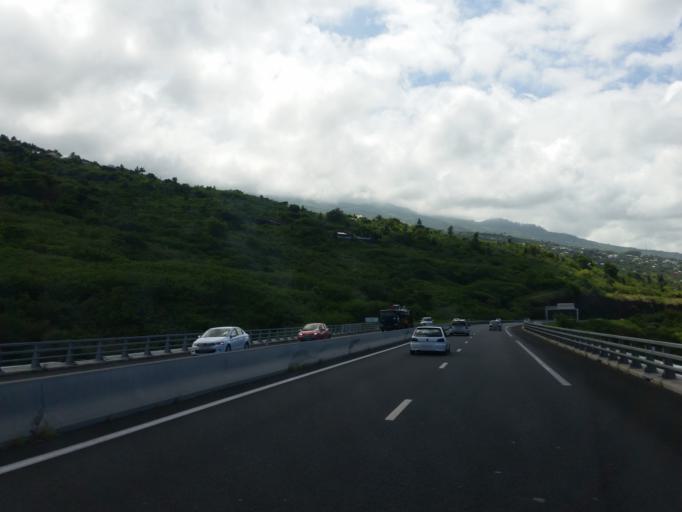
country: RE
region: Reunion
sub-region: Reunion
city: Saint-Leu
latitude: -21.1535
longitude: 55.2927
